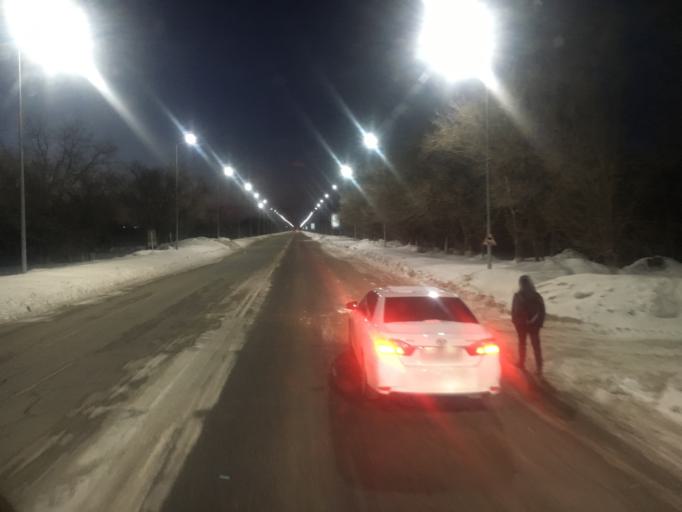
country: KZ
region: Batys Qazaqstan
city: Oral
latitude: 51.1544
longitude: 51.5376
